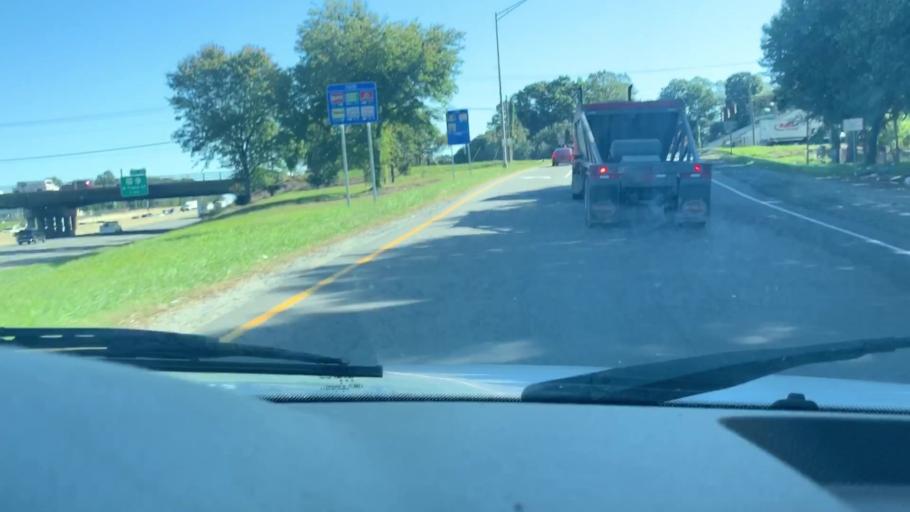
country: US
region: North Carolina
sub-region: Mecklenburg County
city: Charlotte
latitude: 35.2781
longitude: -80.7948
